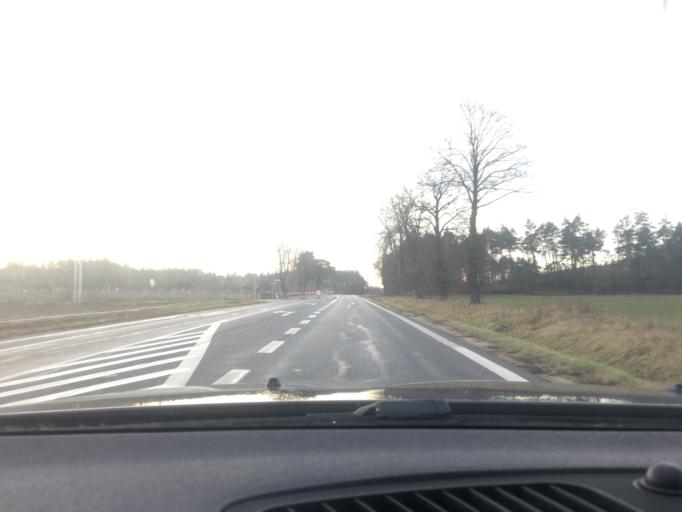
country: PL
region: Swietokrzyskie
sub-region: Powiat jedrzejowski
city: Jedrzejow
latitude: 50.6923
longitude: 20.3624
